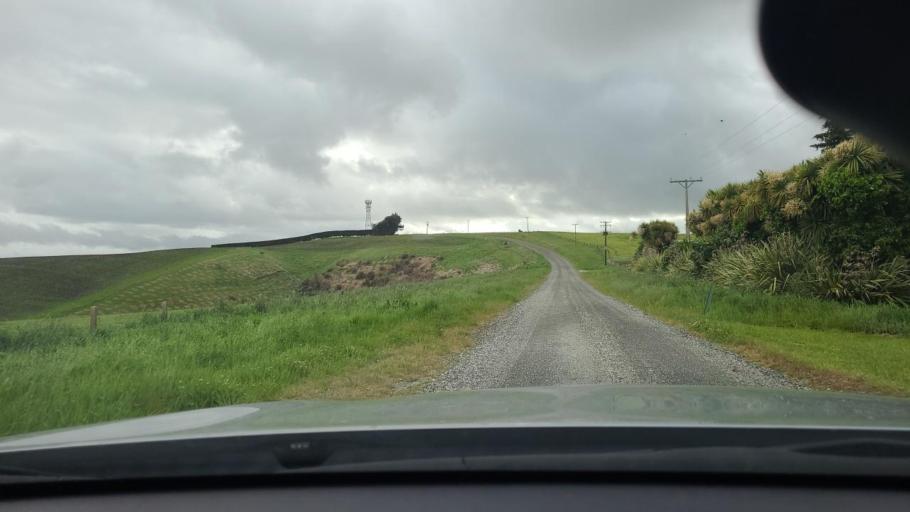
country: NZ
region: Southland
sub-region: Gore District
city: Gore
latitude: -46.5364
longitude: 168.8149
